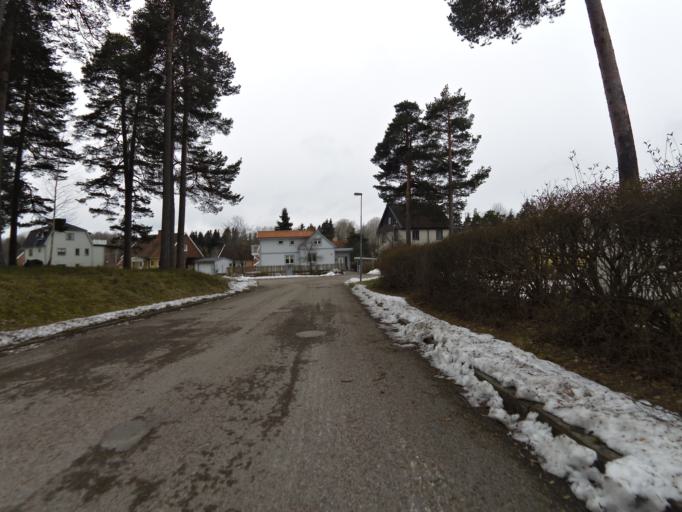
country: SE
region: Gaevleborg
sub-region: Gavle Kommun
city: Gavle
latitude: 60.6646
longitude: 17.1193
